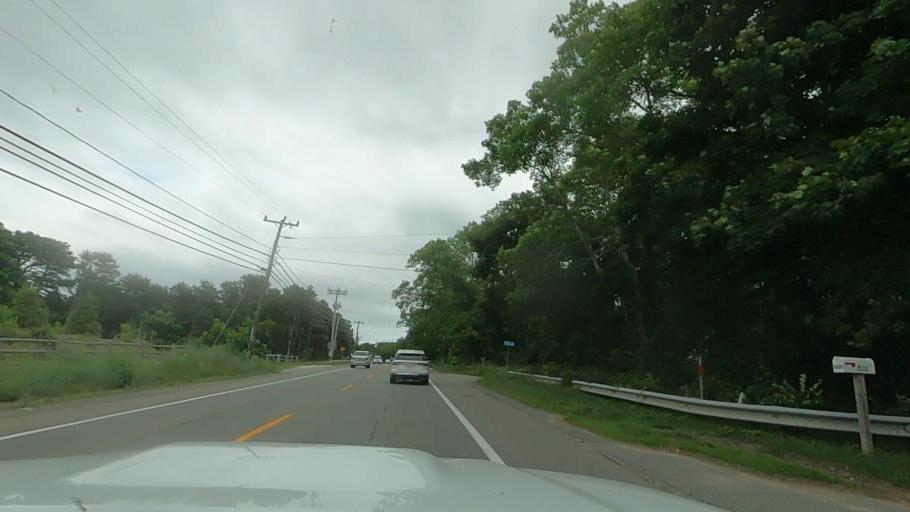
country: US
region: Massachusetts
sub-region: Barnstable County
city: Wellfleet
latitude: 41.9328
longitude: -70.0194
